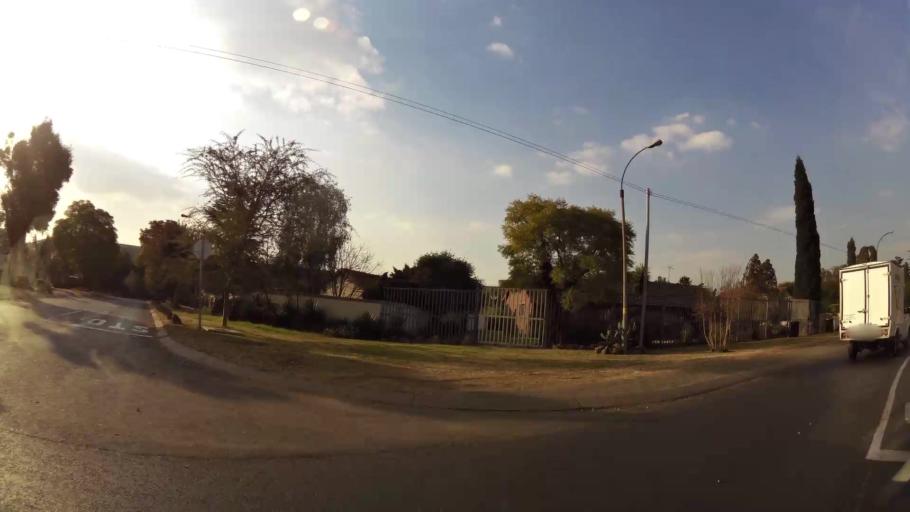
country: ZA
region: Gauteng
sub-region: City of Johannesburg Metropolitan Municipality
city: Modderfontein
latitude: -26.1266
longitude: 28.1896
